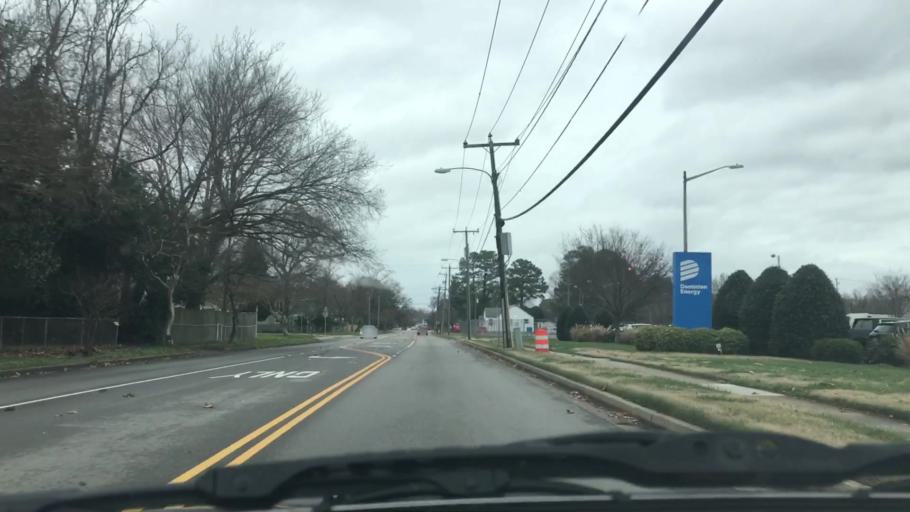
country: US
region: Virginia
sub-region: City of Norfolk
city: Norfolk
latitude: 36.8800
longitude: -76.2543
